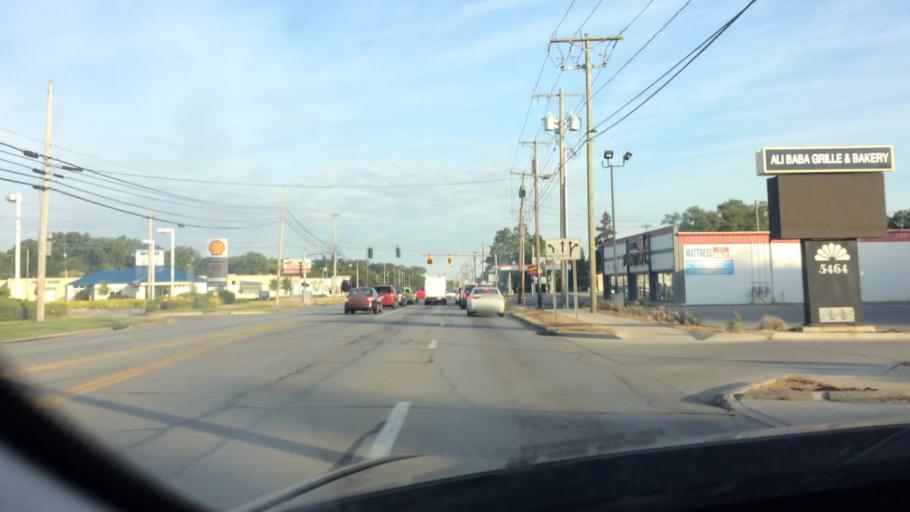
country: US
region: Ohio
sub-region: Lucas County
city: Ottawa Hills
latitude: 41.7059
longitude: -83.6640
